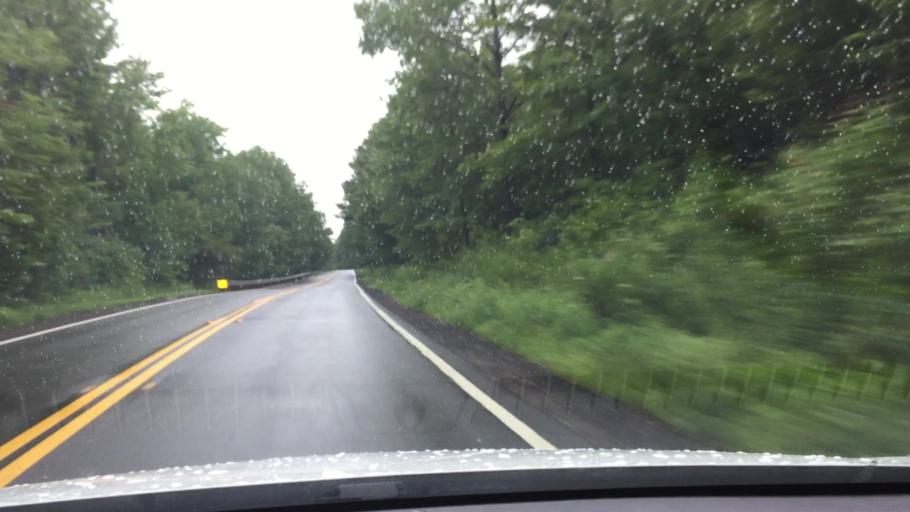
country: US
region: Massachusetts
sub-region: Berkshire County
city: Becket
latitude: 42.3680
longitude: -73.1453
